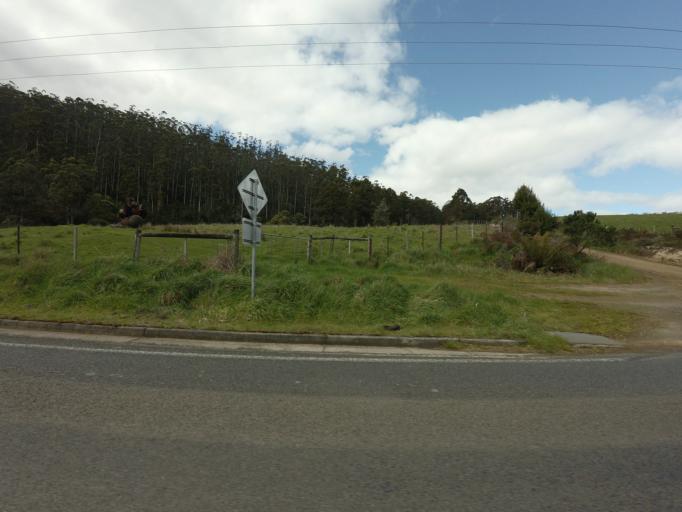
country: AU
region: Tasmania
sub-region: Huon Valley
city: Cygnet
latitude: -43.2829
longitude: 147.0108
